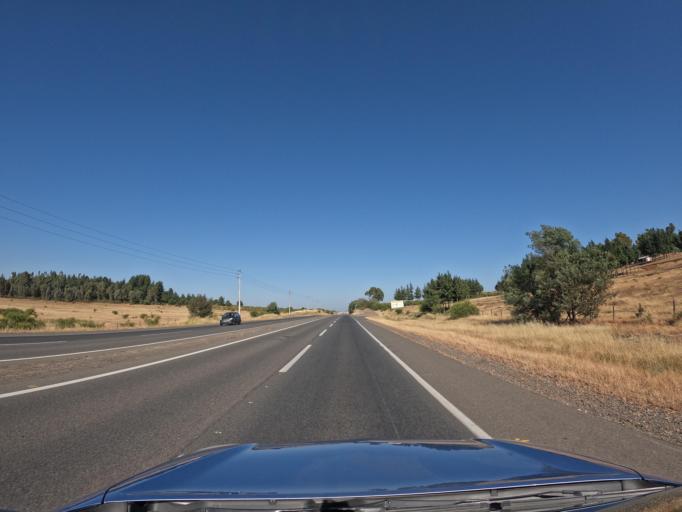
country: CL
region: Biobio
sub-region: Provincia de Nuble
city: Bulnes
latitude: -36.6588
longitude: -72.2919
